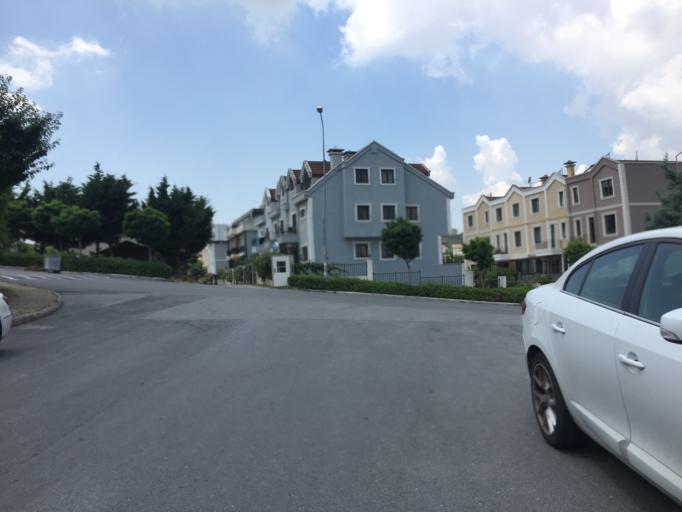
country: TR
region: Istanbul
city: Esenyurt
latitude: 41.0804
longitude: 28.6676
